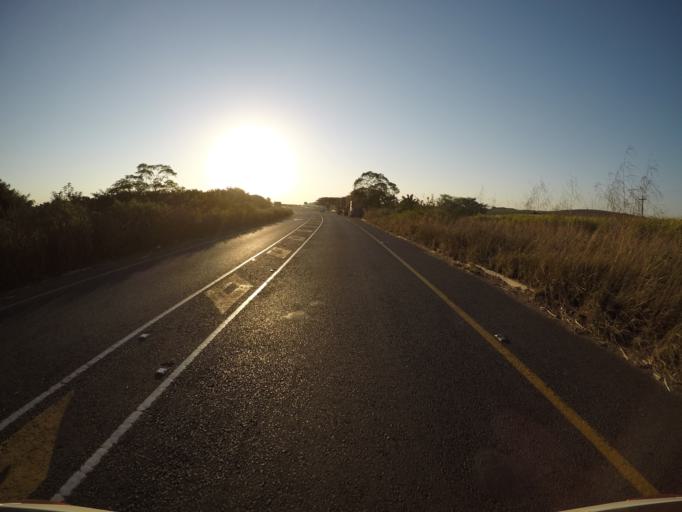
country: ZA
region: KwaZulu-Natal
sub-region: uThungulu District Municipality
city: eSikhawini
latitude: -28.9478
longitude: 31.7320
